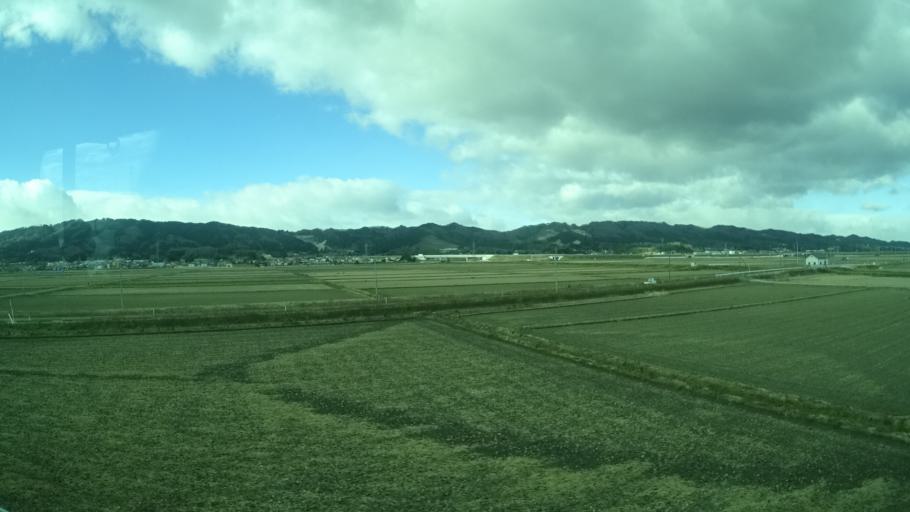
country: JP
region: Miyagi
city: Watari
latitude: 37.9772
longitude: 140.8864
